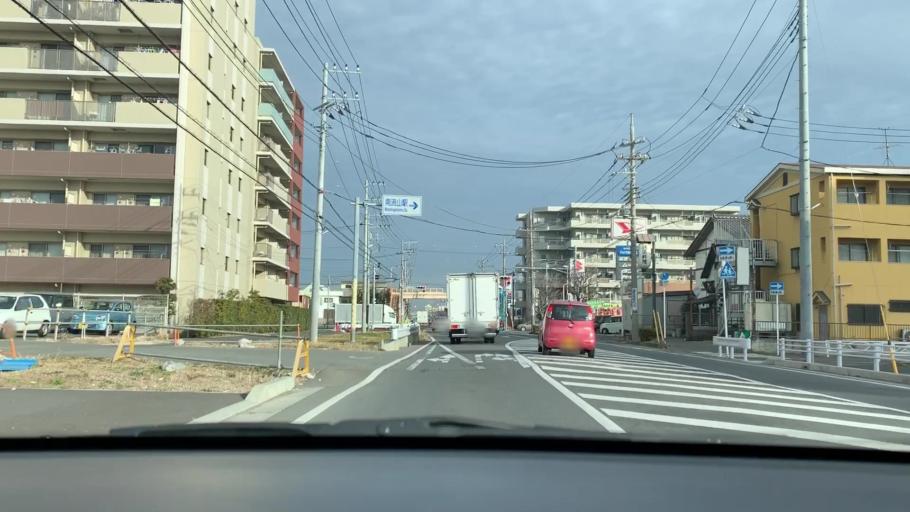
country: JP
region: Chiba
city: Nagareyama
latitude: 35.8353
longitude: 139.8961
